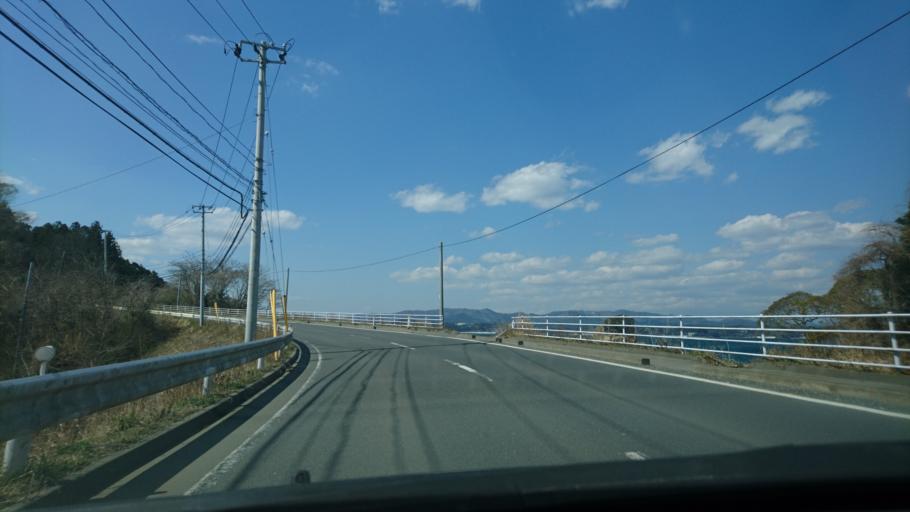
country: JP
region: Miyagi
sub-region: Oshika Gun
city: Onagawa Cho
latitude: 38.6427
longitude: 141.4806
